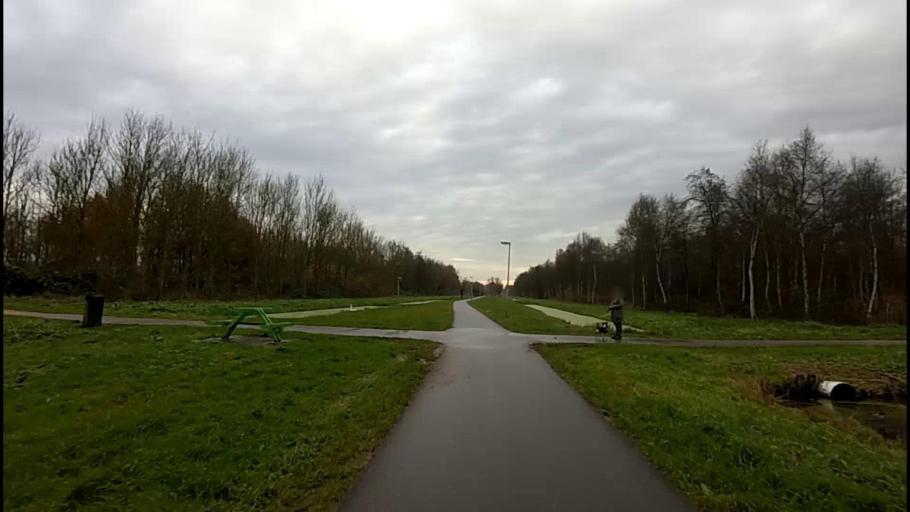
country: NL
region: South Holland
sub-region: Gemeente Krimpen aan den IJssel
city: Krimpen aan den IJssel
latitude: 51.9087
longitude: 4.6353
